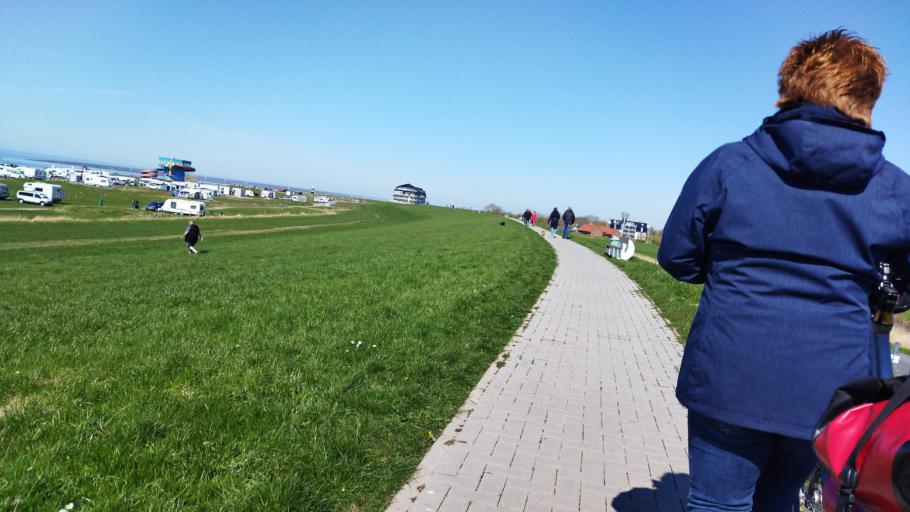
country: DE
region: Lower Saxony
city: Wremen
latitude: 53.6416
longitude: 8.4989
